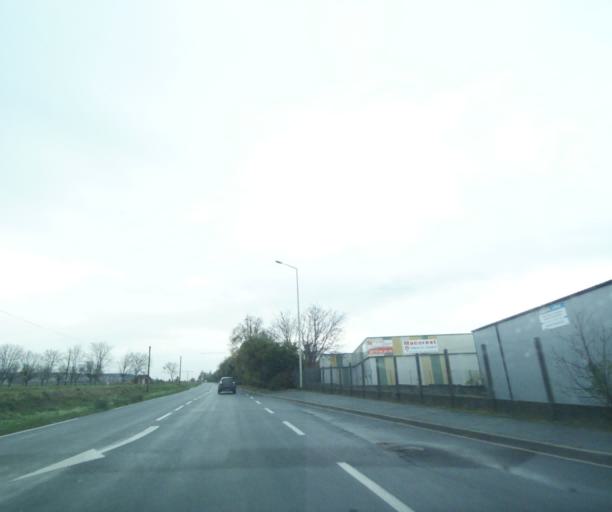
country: FR
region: Auvergne
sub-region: Departement du Puy-de-Dome
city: Perignat-les-Sarlieve
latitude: 45.7510
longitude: 3.1618
